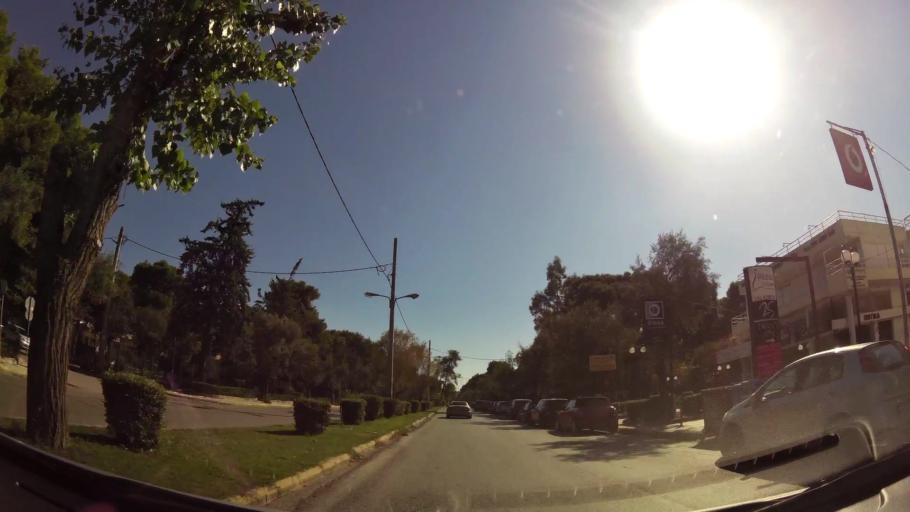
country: GR
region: Attica
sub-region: Nomarchia Athinas
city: Kifisia
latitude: 38.0901
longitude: 23.7976
